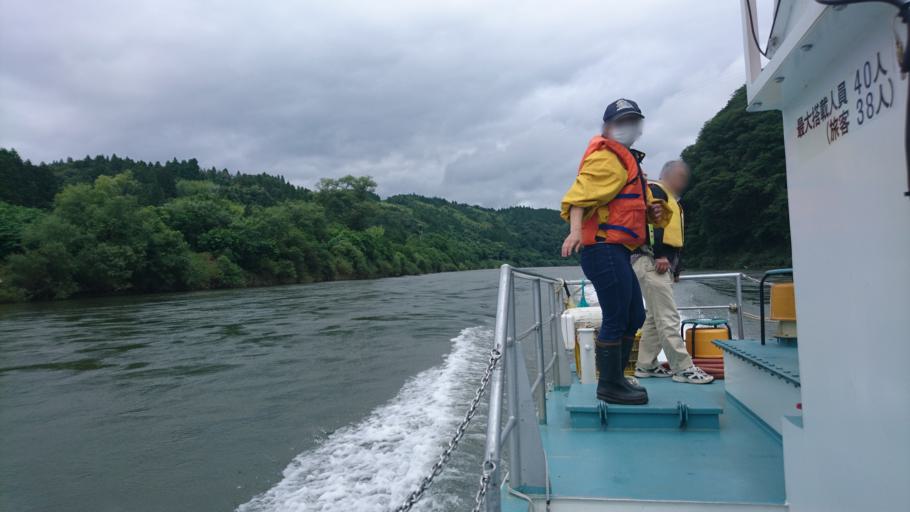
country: JP
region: Iwate
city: Ichinoseki
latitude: 38.9494
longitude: 141.1860
